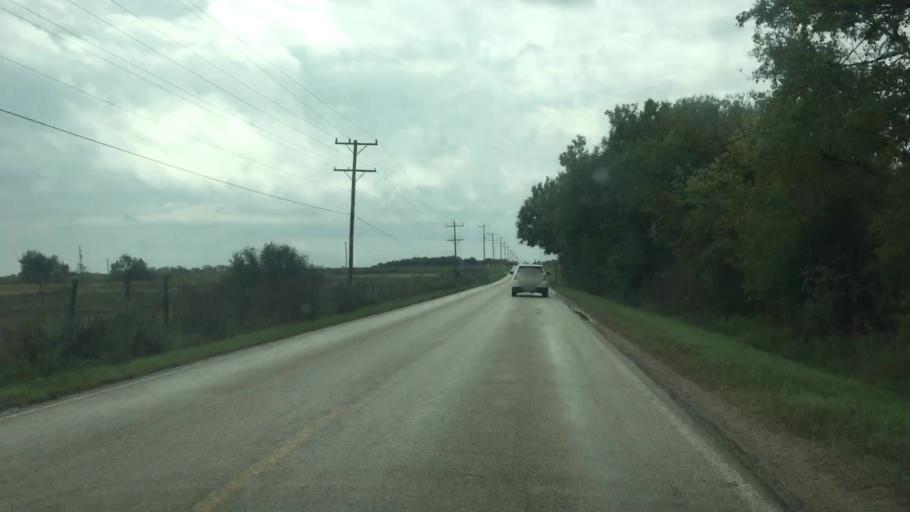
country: US
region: Kansas
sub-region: Allen County
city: Humboldt
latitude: 37.8514
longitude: -95.4369
